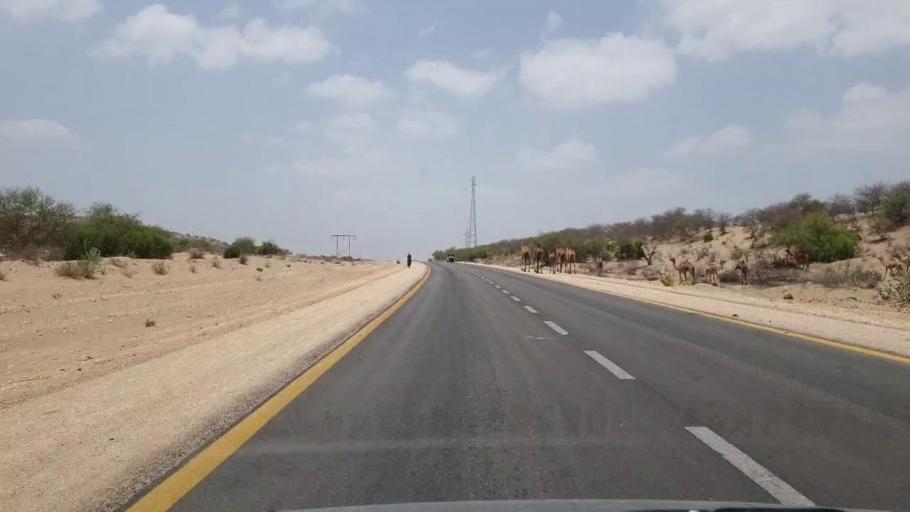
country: PK
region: Sindh
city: Mithi
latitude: 24.8322
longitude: 69.6252
